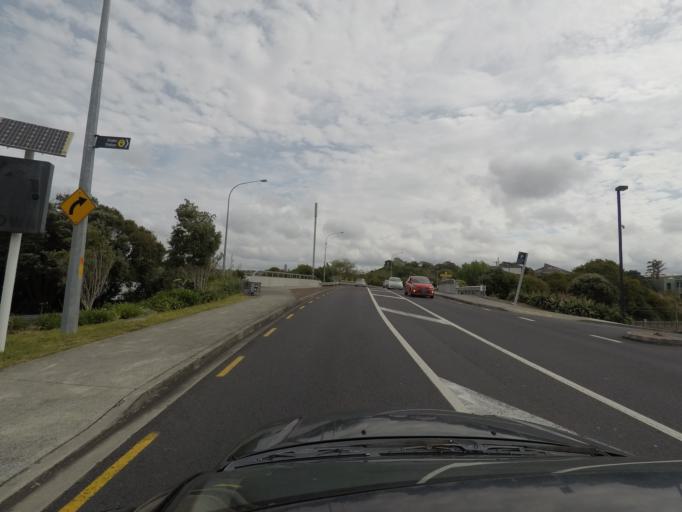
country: NZ
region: Auckland
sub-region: Auckland
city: Auckland
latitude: -36.8626
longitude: 174.8117
